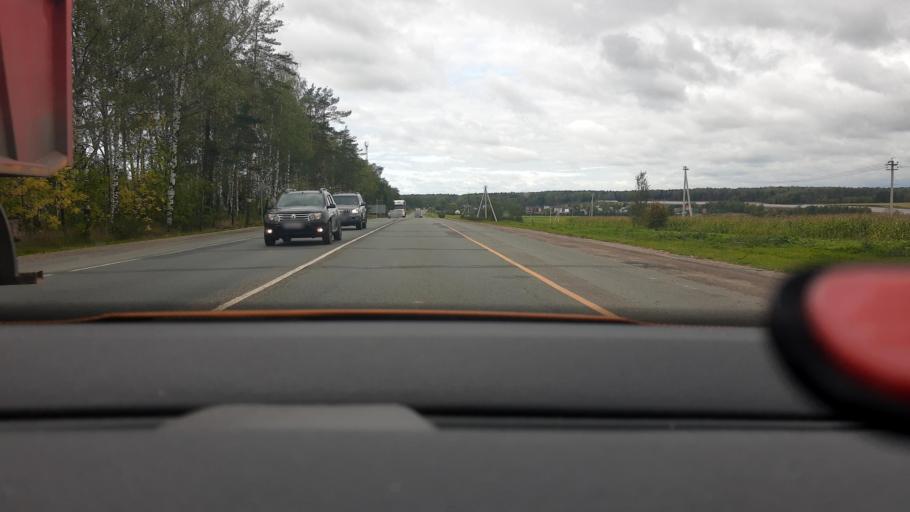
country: RU
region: Moskovskaya
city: Krasnoarmeysk
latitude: 56.0766
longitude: 38.0412
